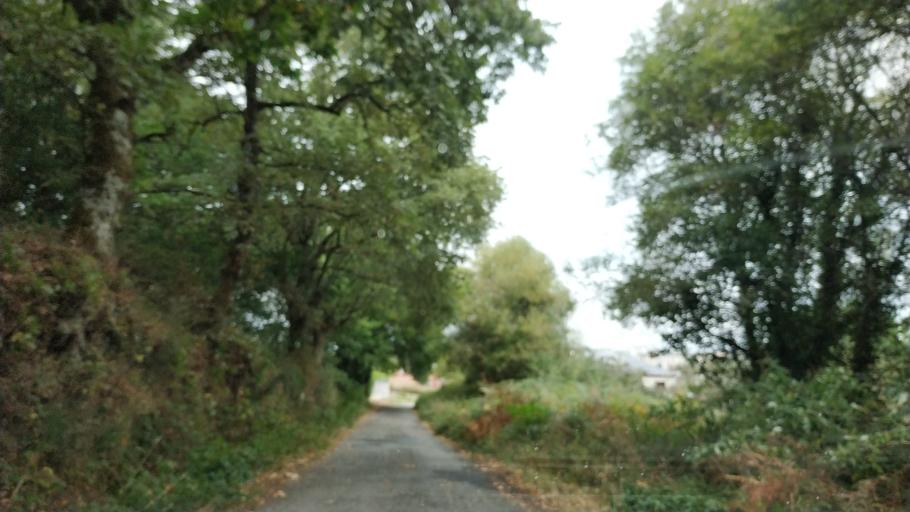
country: ES
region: Galicia
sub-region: Provincia de Lugo
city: Lugo
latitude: 42.9986
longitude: -7.5752
